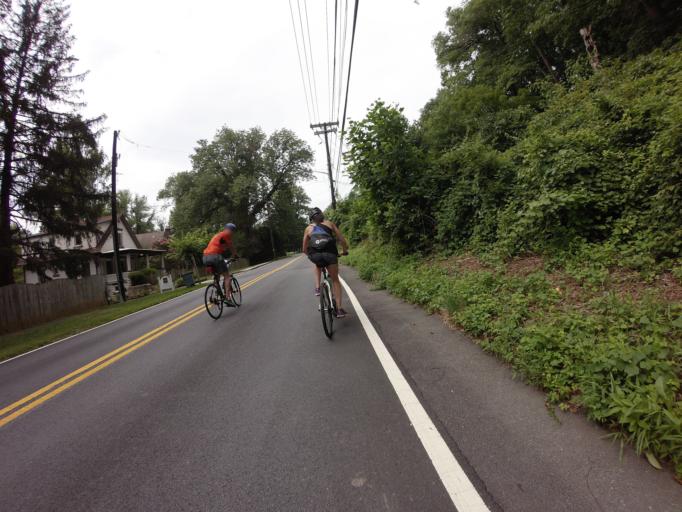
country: US
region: Maryland
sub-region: Montgomery County
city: Forest Glen
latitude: 39.0013
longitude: -77.0648
